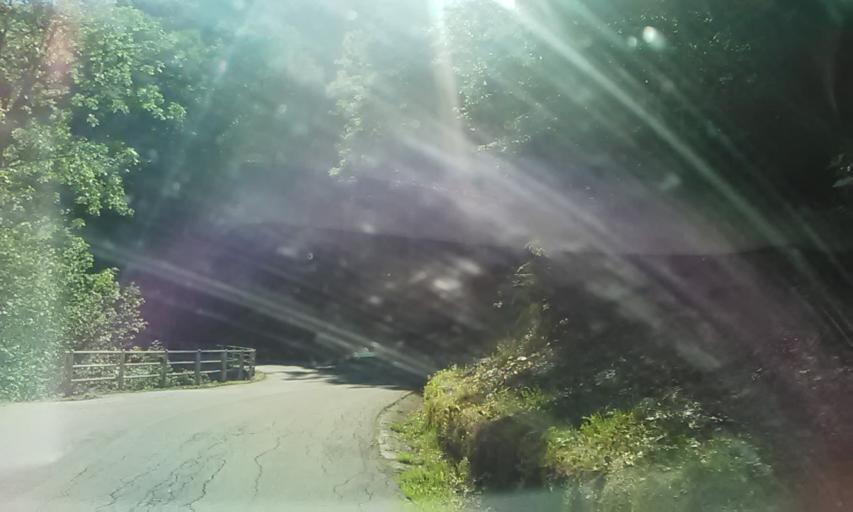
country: IT
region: Piedmont
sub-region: Provincia di Vercelli
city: Varallo
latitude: 45.8405
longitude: 8.2786
